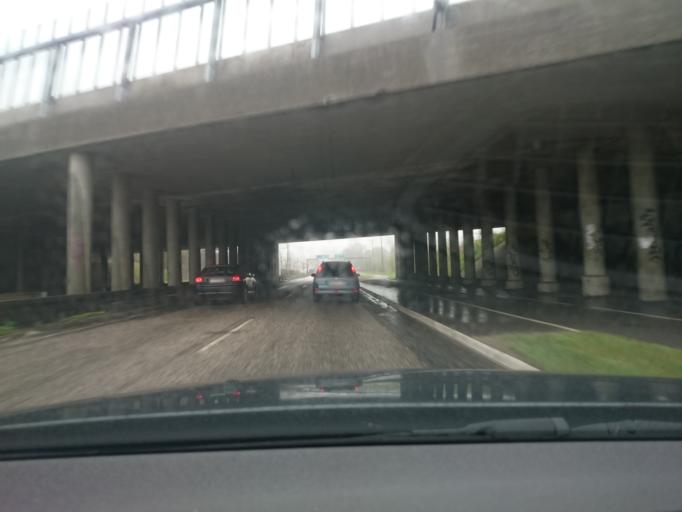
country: DK
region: Capital Region
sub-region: Herlev Kommune
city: Herlev
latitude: 55.7337
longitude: 12.4553
